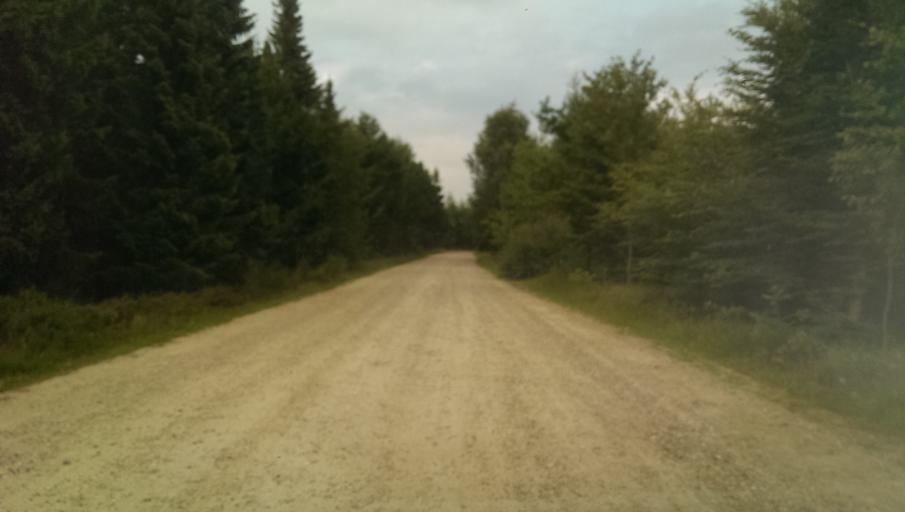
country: DK
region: South Denmark
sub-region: Varde Kommune
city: Varde
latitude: 55.5895
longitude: 8.5386
